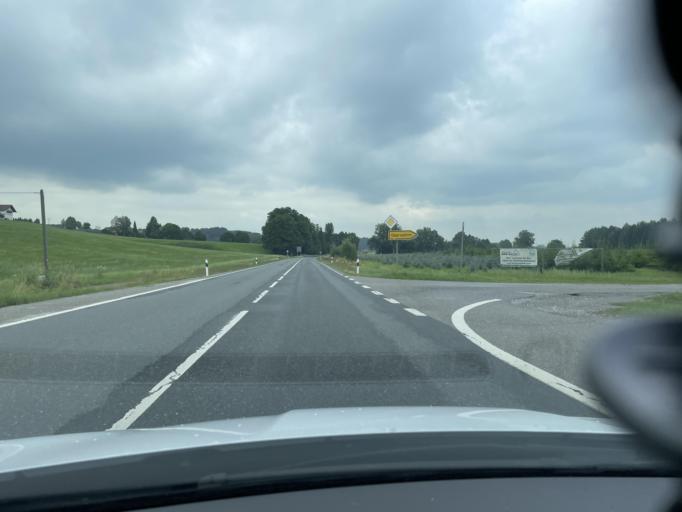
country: DE
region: Bavaria
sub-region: Upper Bavaria
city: Schechen
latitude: 47.9552
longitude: 12.1268
